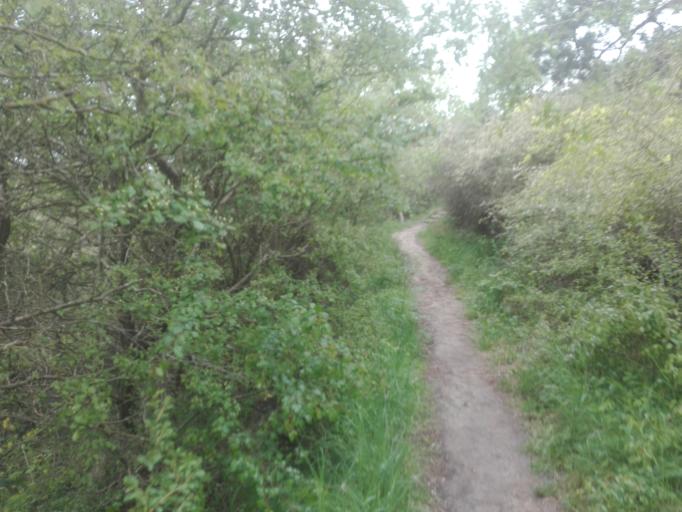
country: DK
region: Central Jutland
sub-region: Syddjurs Kommune
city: Ebeltoft
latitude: 56.0993
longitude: 10.5261
